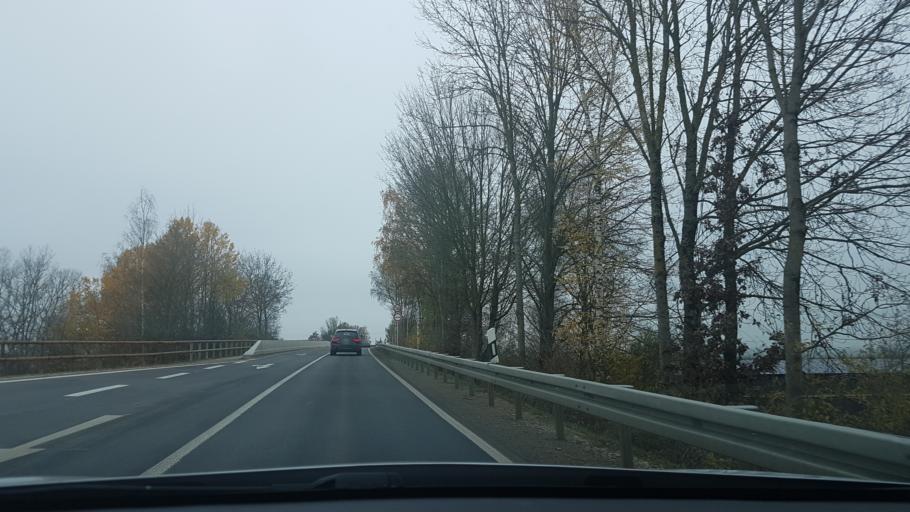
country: DE
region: Bavaria
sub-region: Lower Bavaria
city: Essenbach
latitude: 48.6019
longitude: 12.2362
